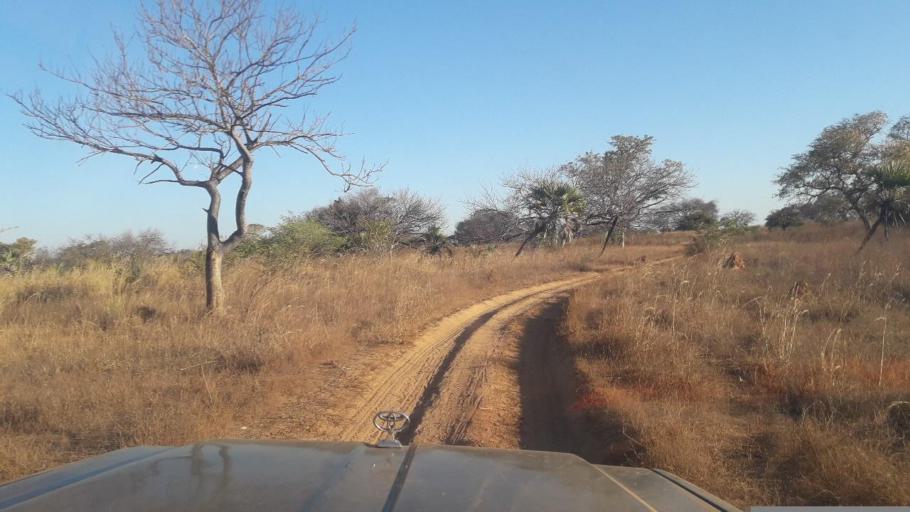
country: MG
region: Boeny
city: Sitampiky
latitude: -16.5011
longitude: 45.6031
